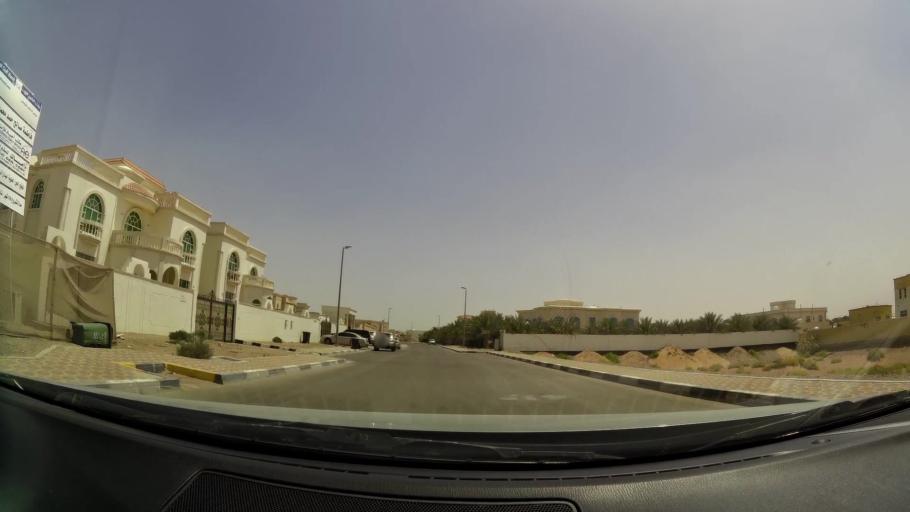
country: AE
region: Abu Dhabi
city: Al Ain
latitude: 24.2615
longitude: 55.6991
